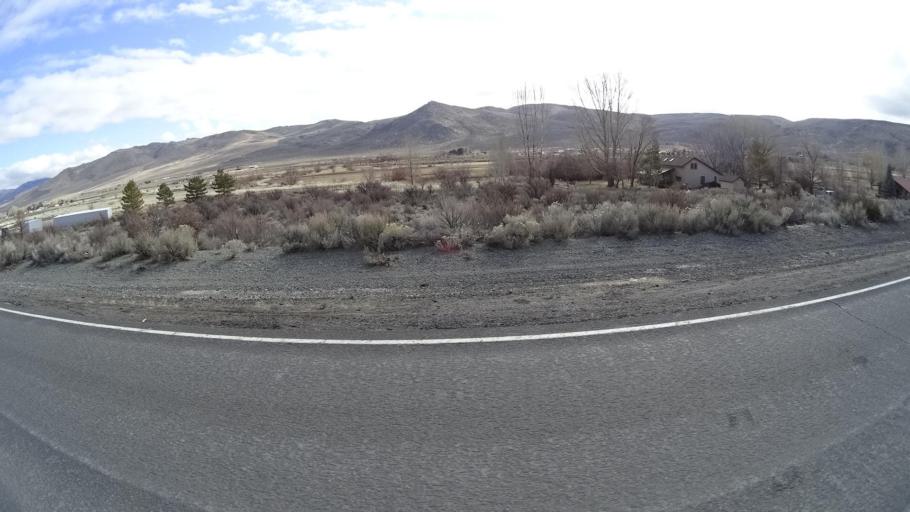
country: US
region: Nevada
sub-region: Washoe County
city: Cold Springs
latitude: 39.8523
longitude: -119.9351
